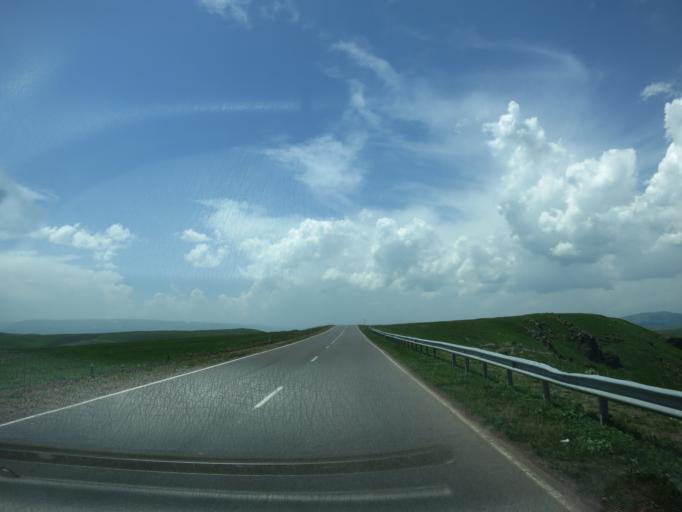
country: GE
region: Samtskhe-Javakheti
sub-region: Ninotsminda
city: Ninotsminda
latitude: 41.2918
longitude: 43.7209
